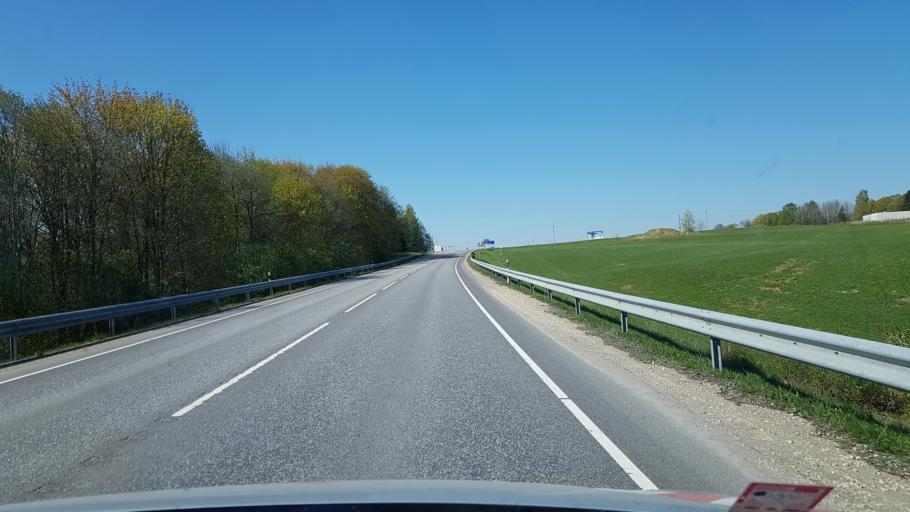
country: EE
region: Vorumaa
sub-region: Antsla vald
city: Vana-Antsla
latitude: 57.9843
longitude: 26.7700
